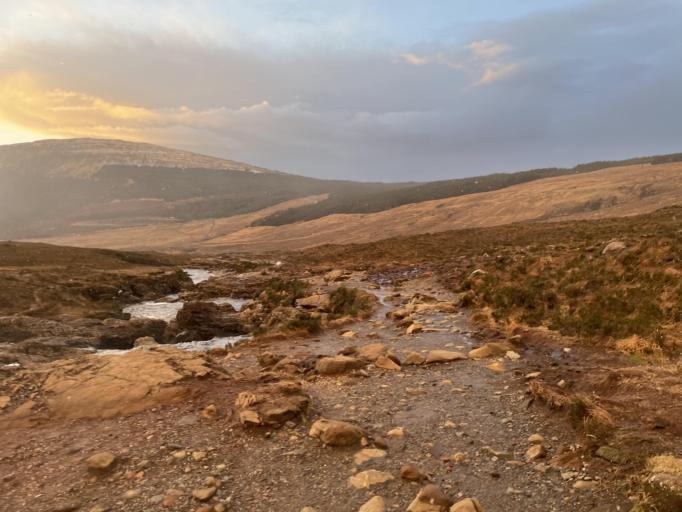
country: GB
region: Scotland
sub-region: Highland
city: Isle of Skye
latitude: 57.2492
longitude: -6.2486
